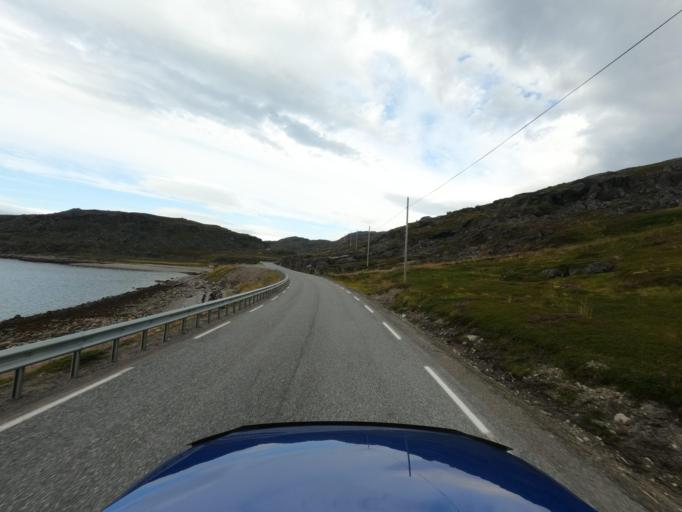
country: NO
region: Finnmark Fylke
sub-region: Hammerfest
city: Rypefjord
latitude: 70.5930
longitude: 23.6817
